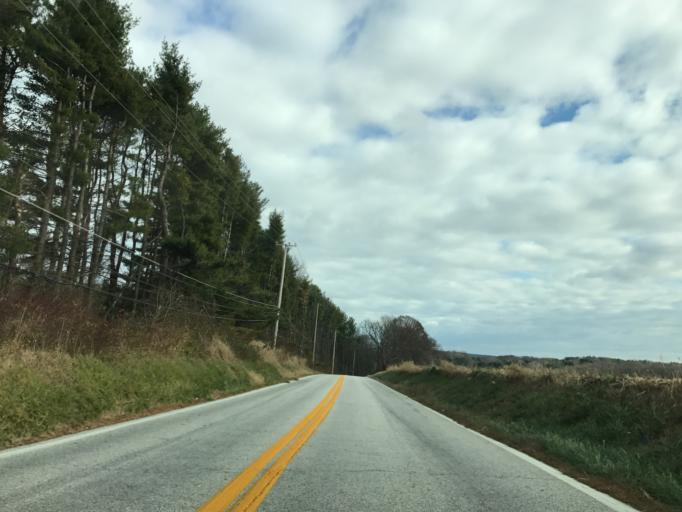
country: US
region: Maryland
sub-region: Harford County
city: Jarrettsville
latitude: 39.5113
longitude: -76.5180
